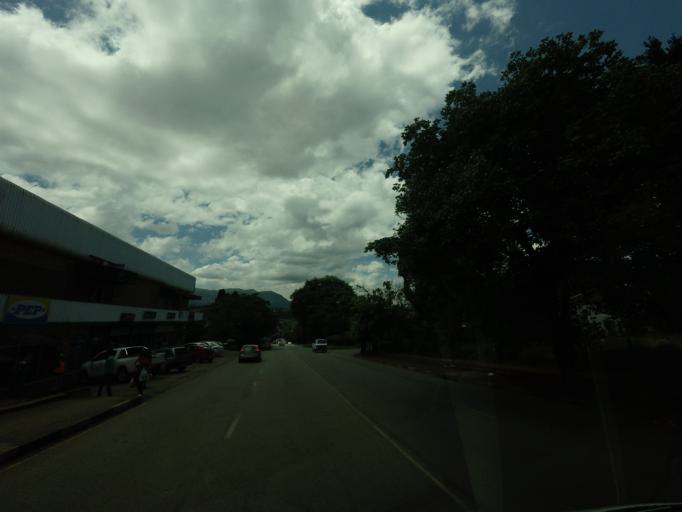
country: ZA
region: Mpumalanga
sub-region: Ehlanzeni District
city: Graksop
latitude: -25.0957
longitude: 30.7785
